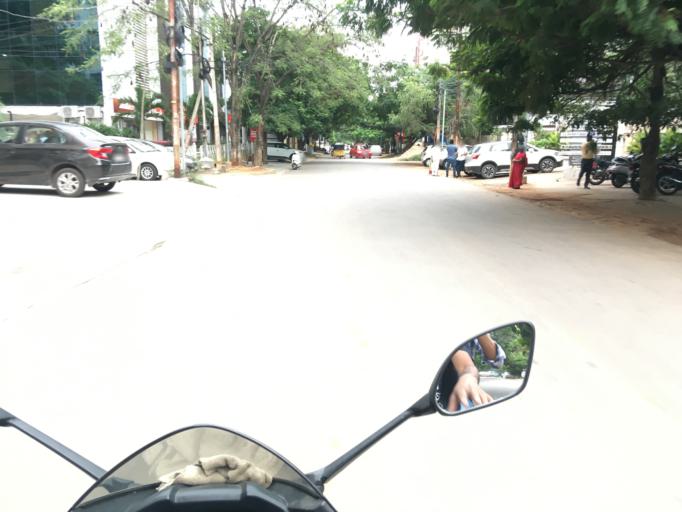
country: IN
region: Telangana
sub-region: Rangareddi
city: Kukatpalli
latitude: 17.4509
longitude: 78.3857
